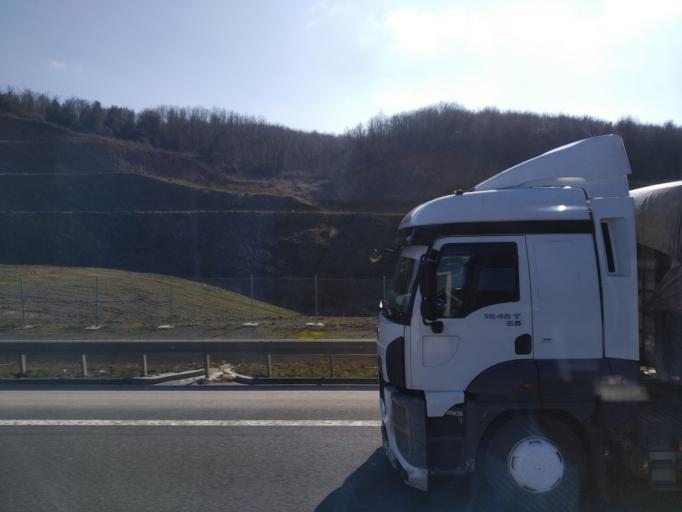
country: TR
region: Istanbul
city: Arikoey
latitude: 41.2311
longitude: 28.9444
